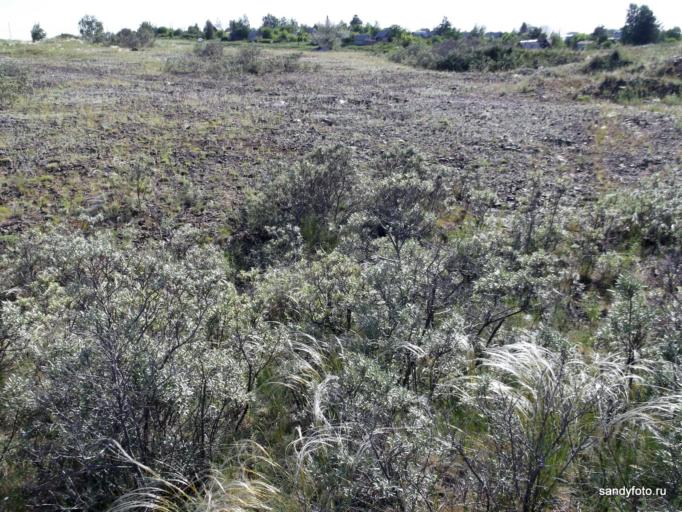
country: RU
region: Chelyabinsk
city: Troitsk
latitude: 54.0642
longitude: 61.5294
